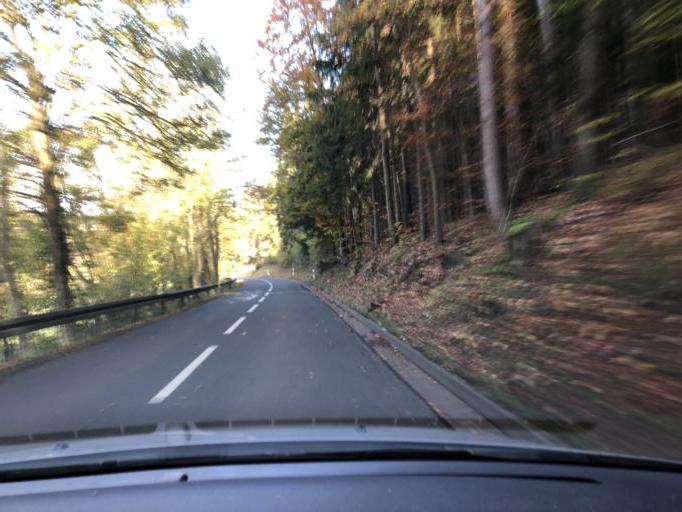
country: DE
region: Thuringia
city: Reurieth
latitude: 50.4431
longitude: 10.6480
